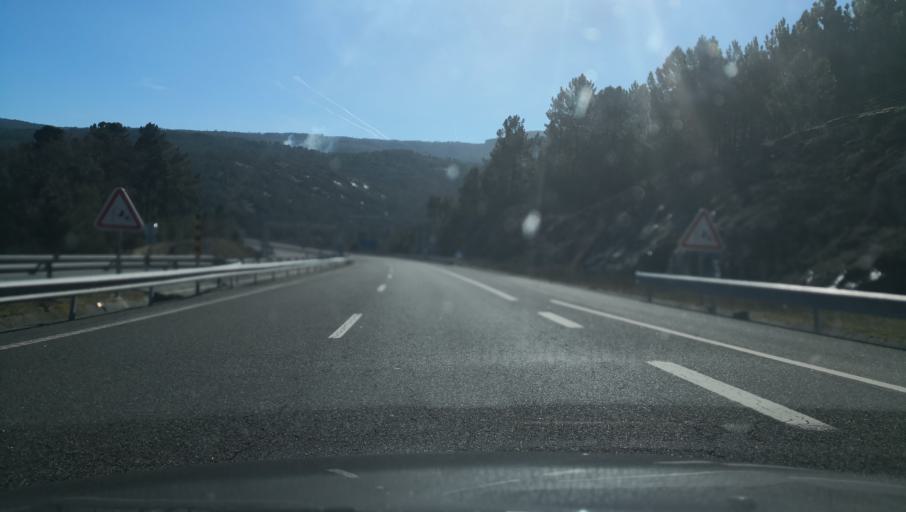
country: PT
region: Vila Real
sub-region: Vila Pouca de Aguiar
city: Vila Pouca de Aguiar
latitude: 41.5809
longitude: -7.6413
